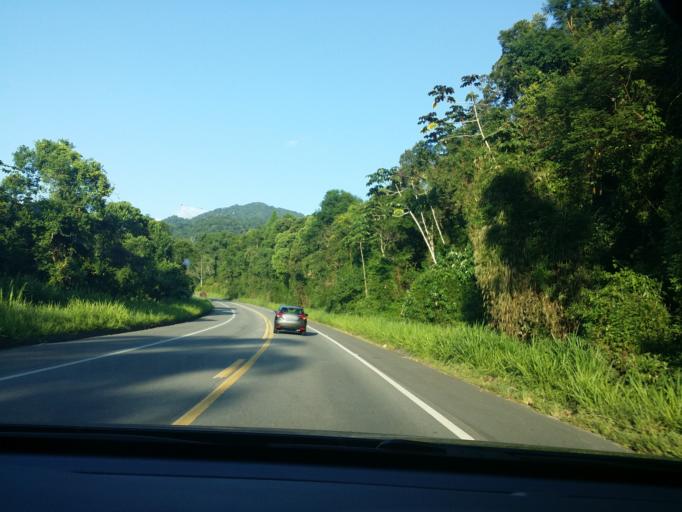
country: BR
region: Sao Paulo
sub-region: Sao Sebastiao
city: Sao Sebastiao
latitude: -23.7473
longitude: -45.7405
